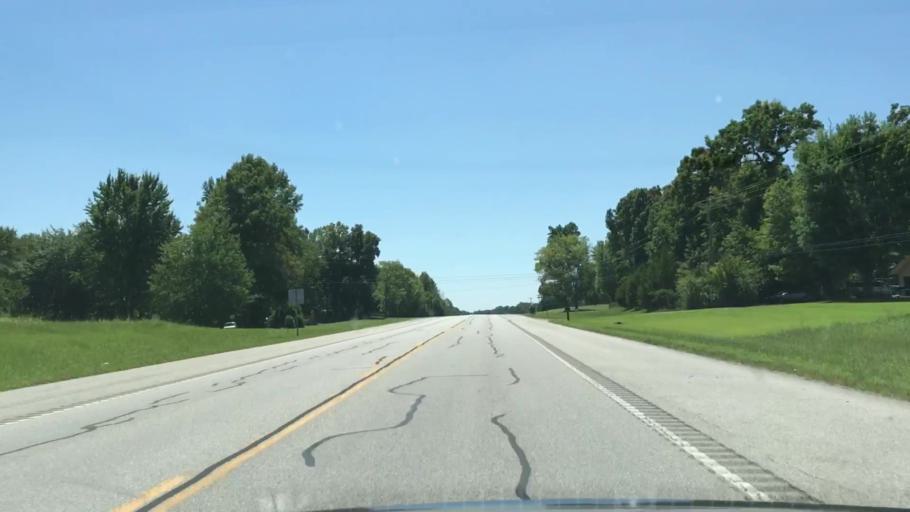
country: US
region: Tennessee
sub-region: Putnam County
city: Baxter
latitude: 36.1818
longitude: -85.6237
